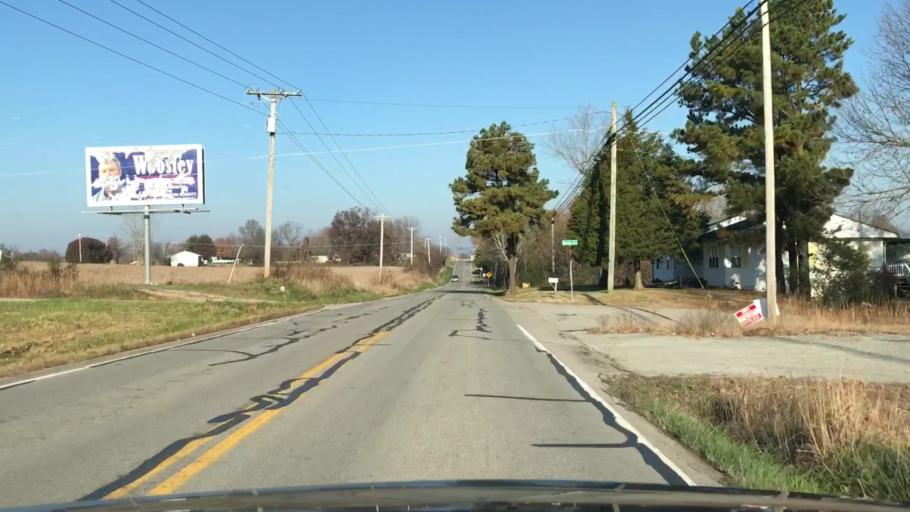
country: US
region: Kentucky
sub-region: Edmonson County
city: Brownsville
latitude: 37.2550
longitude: -86.2804
